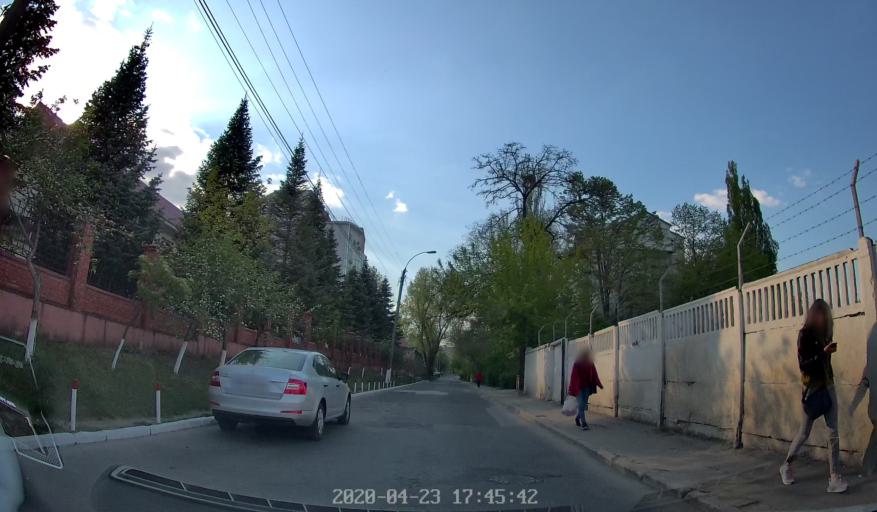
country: MD
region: Chisinau
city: Chisinau
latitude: 46.9967
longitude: 28.8235
